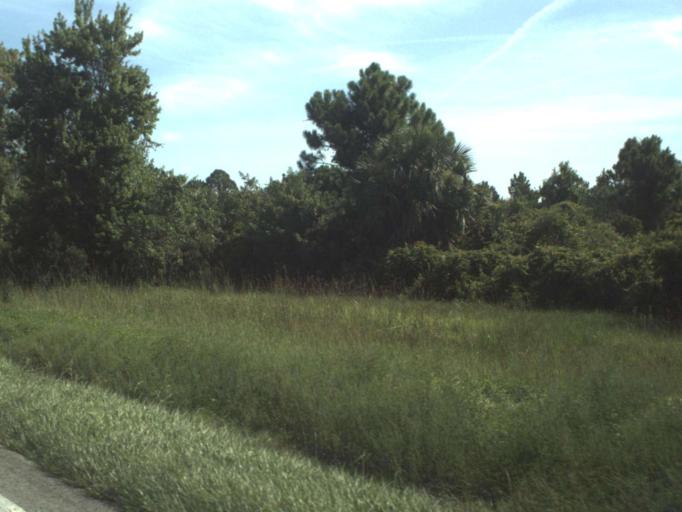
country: US
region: Florida
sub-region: Indian River County
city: Fellsmere
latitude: 27.7299
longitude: -80.5467
